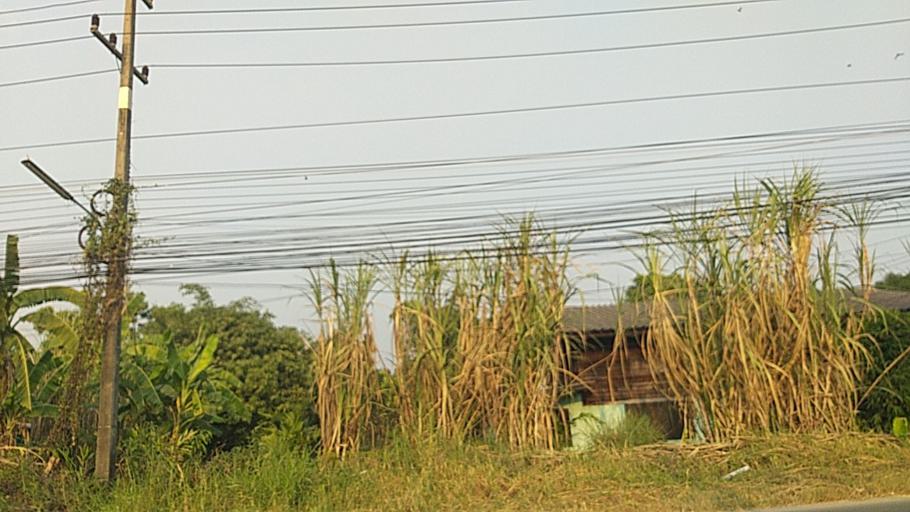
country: TH
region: Nakhon Nayok
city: Ongkharak
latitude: 14.1264
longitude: 100.9942
